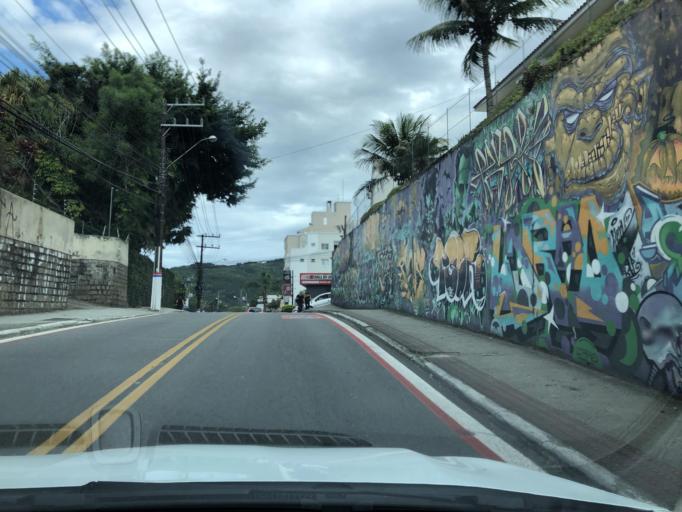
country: BR
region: Santa Catarina
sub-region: Florianopolis
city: Corrego Grande
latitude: -27.5997
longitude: -48.5098
